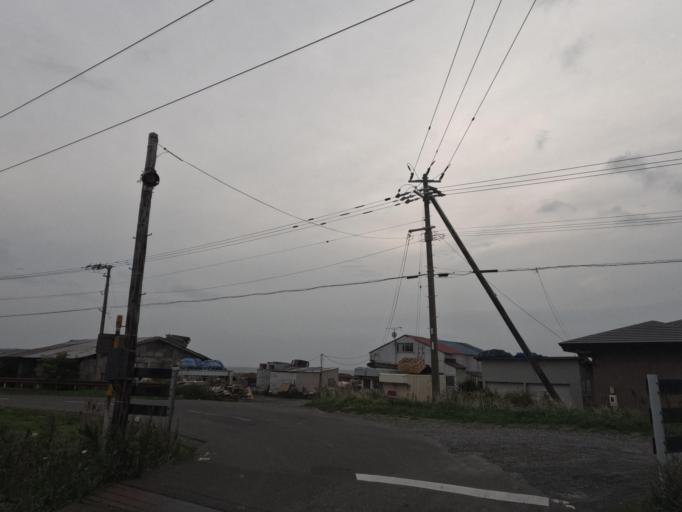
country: JP
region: Hokkaido
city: Date
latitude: 42.3835
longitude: 140.9085
